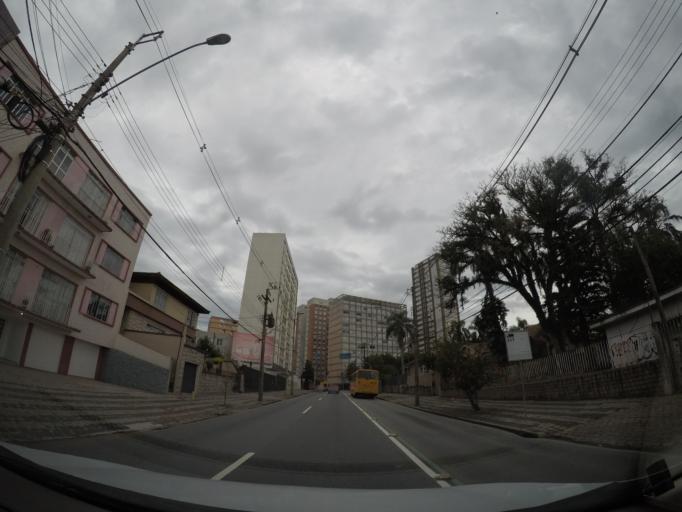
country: BR
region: Parana
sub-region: Curitiba
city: Curitiba
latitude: -25.4264
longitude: -49.2580
